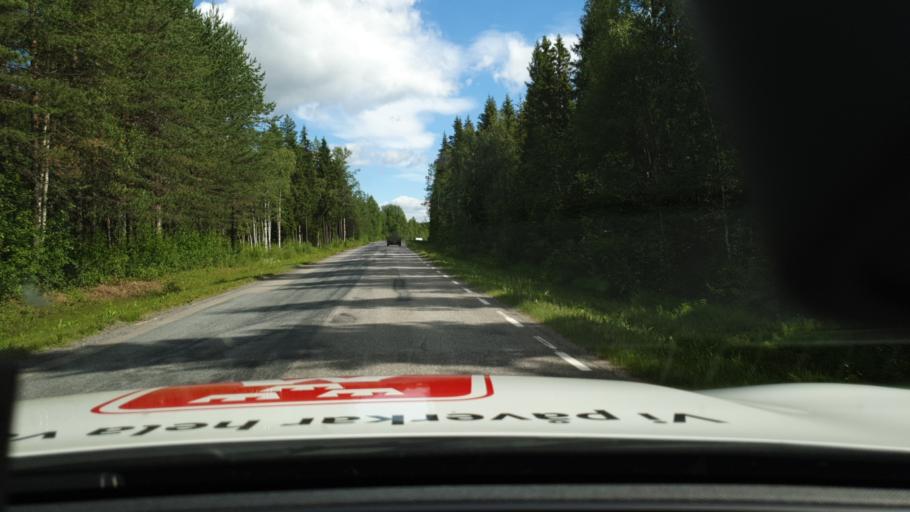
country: SE
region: Norrbotten
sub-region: Lulea Kommun
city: Ranea
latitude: 65.7750
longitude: 22.2055
